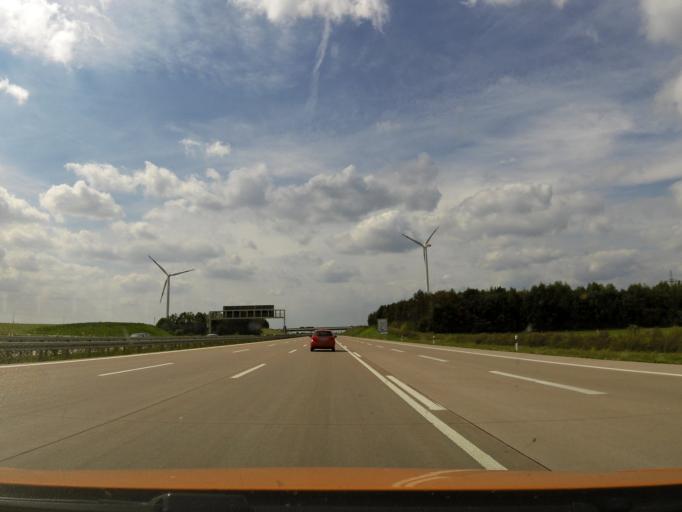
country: DE
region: Berlin
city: Falkenberg
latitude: 52.6151
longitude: 13.5457
